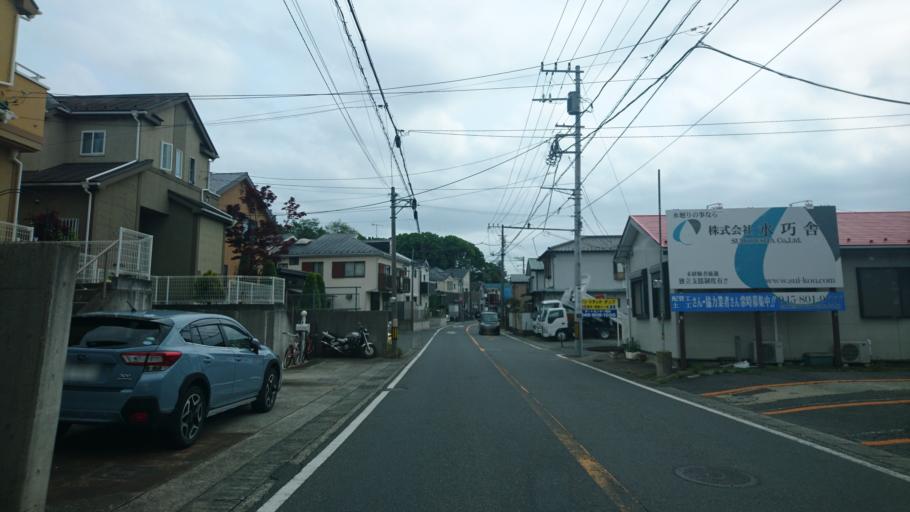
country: JP
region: Kanagawa
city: Minami-rinkan
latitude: 35.4159
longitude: 139.4797
